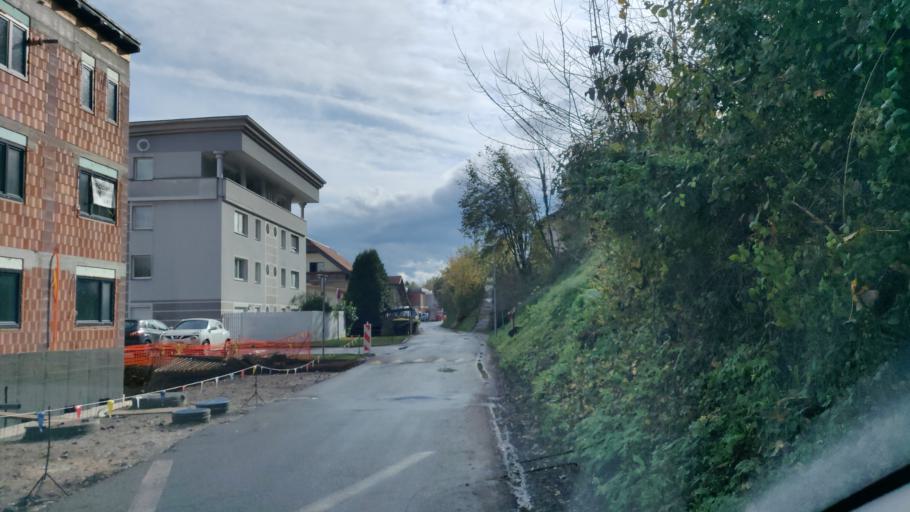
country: SI
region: Trzin
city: Trzin
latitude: 46.1337
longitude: 14.5604
